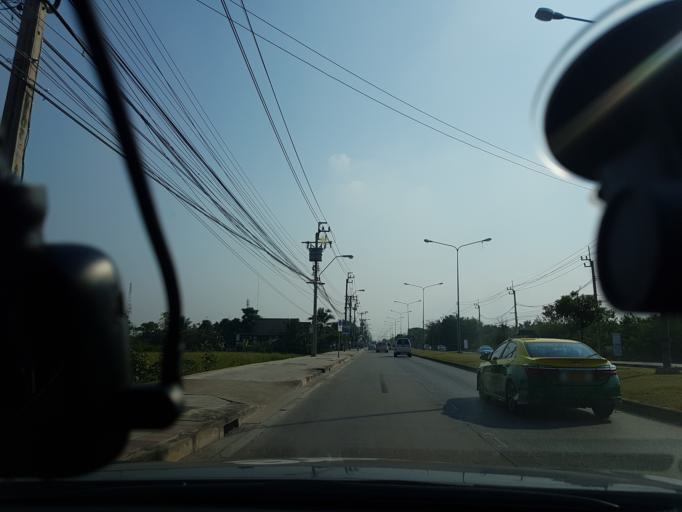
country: TH
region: Bangkok
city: Khlong Sam Wa
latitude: 13.8738
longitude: 100.7225
